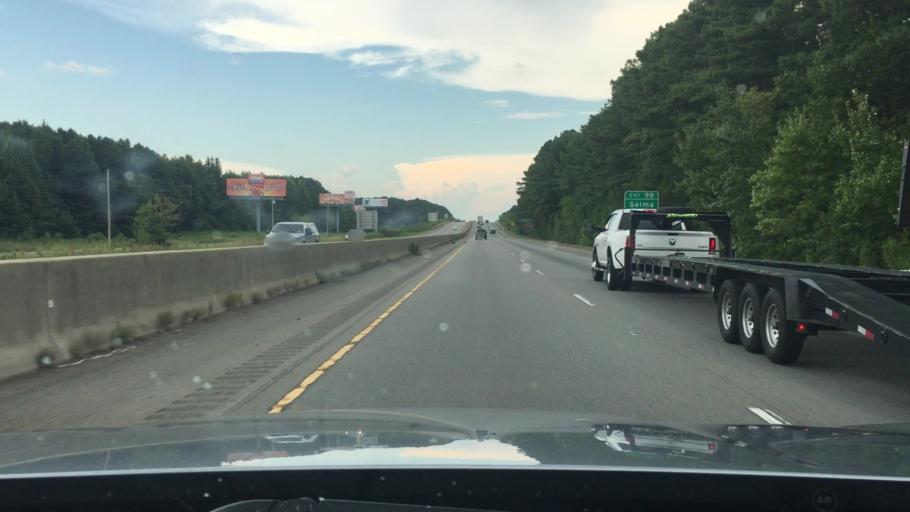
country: US
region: North Carolina
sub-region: Johnston County
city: Selma
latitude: 35.5248
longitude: -78.2786
